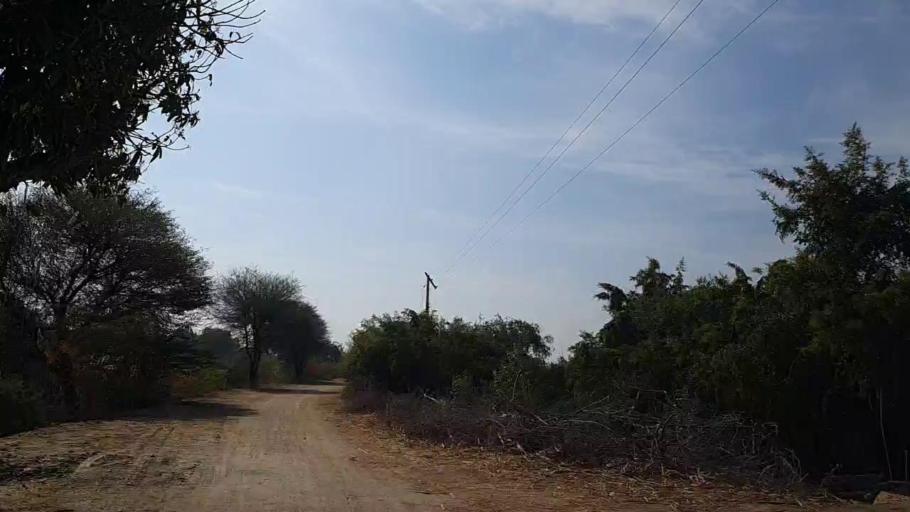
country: PK
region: Sindh
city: Mirpur Khas
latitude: 25.4732
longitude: 68.9745
